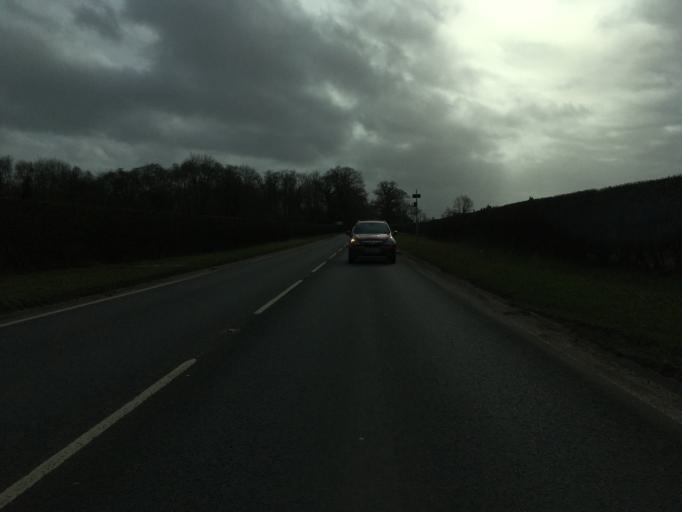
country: GB
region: England
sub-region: West Berkshire
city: Theale
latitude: 51.4545
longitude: -1.0909
